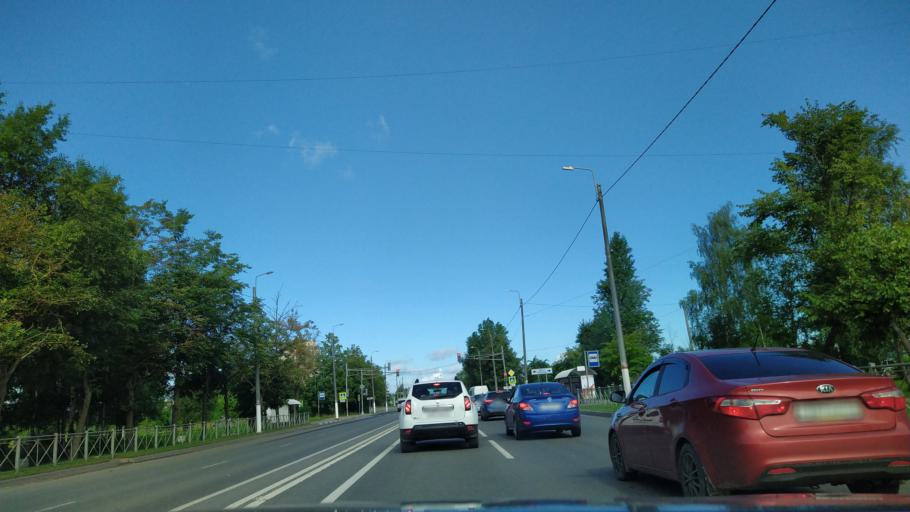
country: RU
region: Leningrad
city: Tosno
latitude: 59.5472
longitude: 30.8658
